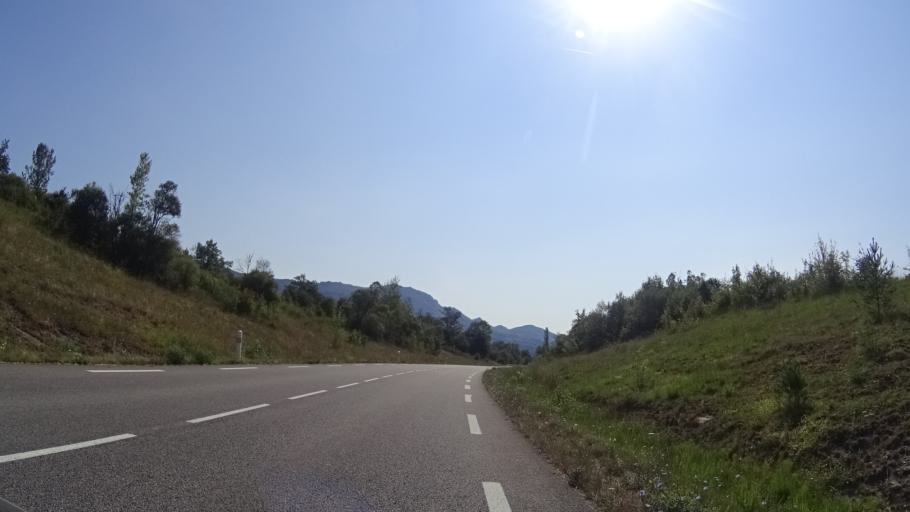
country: FR
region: Midi-Pyrenees
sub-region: Departement de l'Ariege
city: Saint-Paul-de-Jarrat
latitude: 42.9337
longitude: 1.7133
